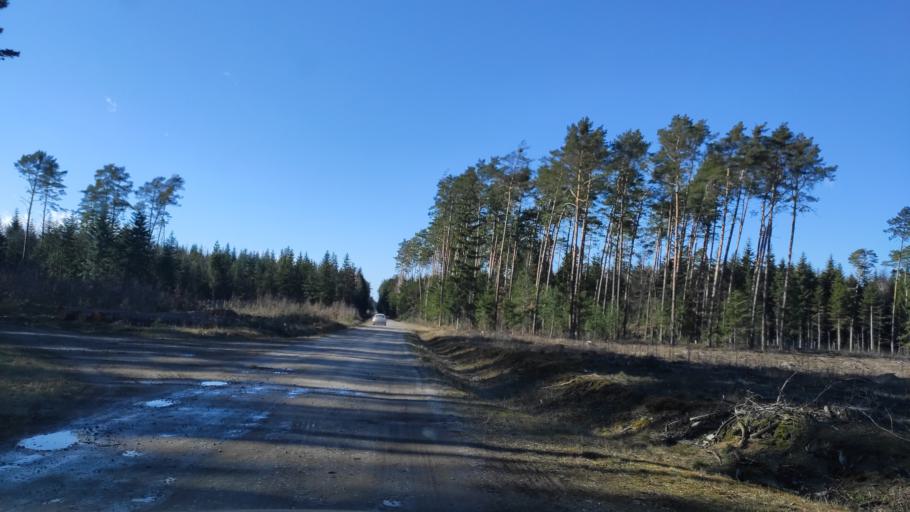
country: PL
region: Masovian Voivodeship
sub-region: Powiat radomski
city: Jedlnia-Letnisko
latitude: 51.4643
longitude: 21.3195
